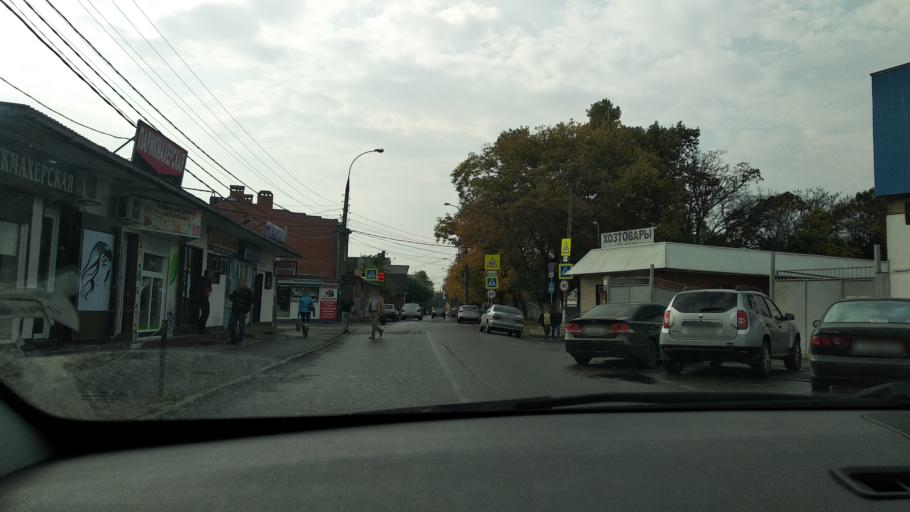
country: RU
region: Krasnodarskiy
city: Krasnodar
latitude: 45.0190
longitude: 38.9993
